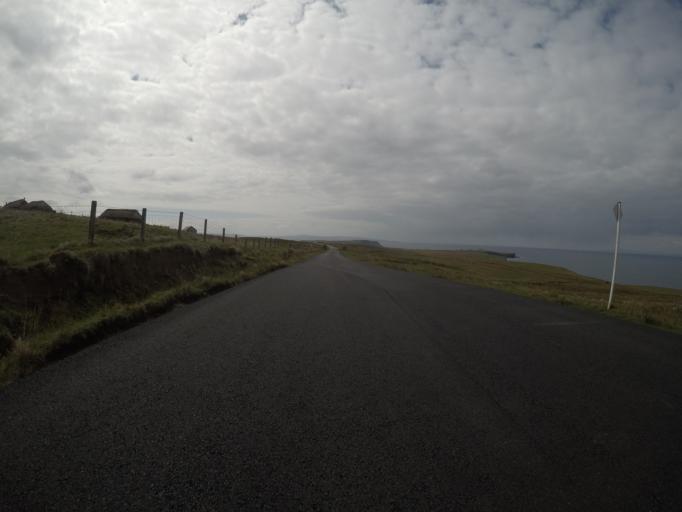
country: GB
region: Scotland
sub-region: Highland
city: Portree
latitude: 57.6610
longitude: -6.3692
